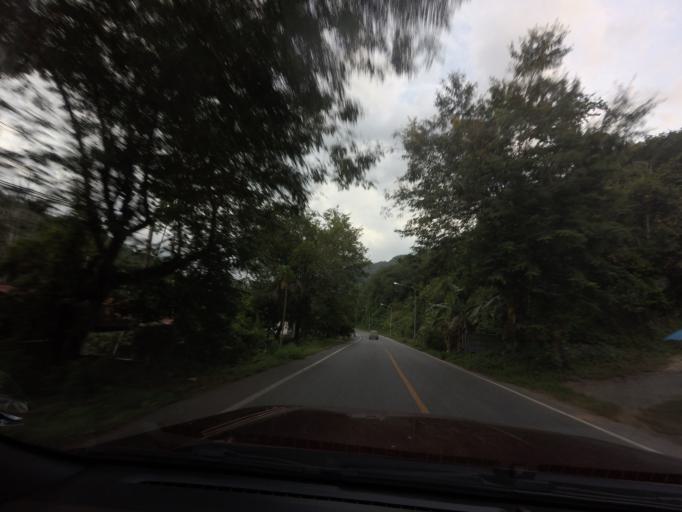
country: TH
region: Yala
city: Than To
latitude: 6.0039
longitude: 101.1940
